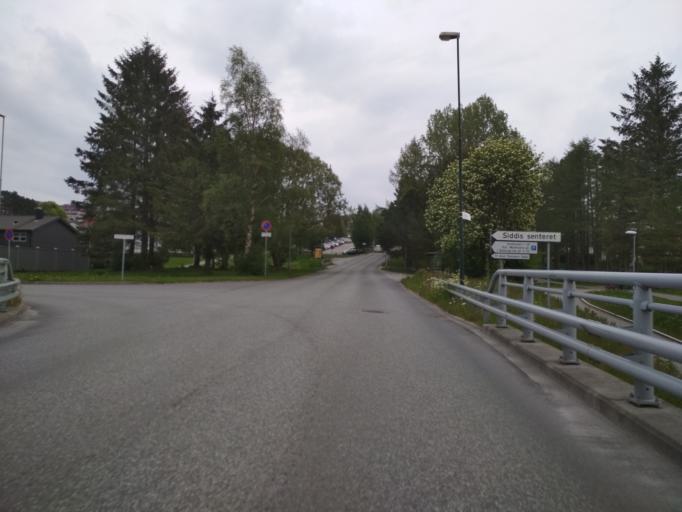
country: NO
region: Rogaland
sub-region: Stavanger
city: Stavanger
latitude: 58.9525
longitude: 5.6879
